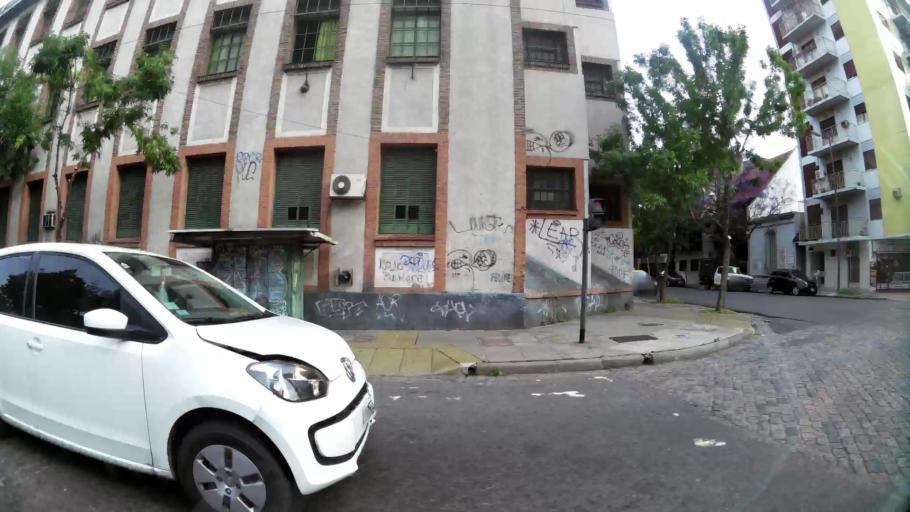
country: AR
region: Buenos Aires F.D.
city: Villa Santa Rita
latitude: -34.6354
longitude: -58.4743
